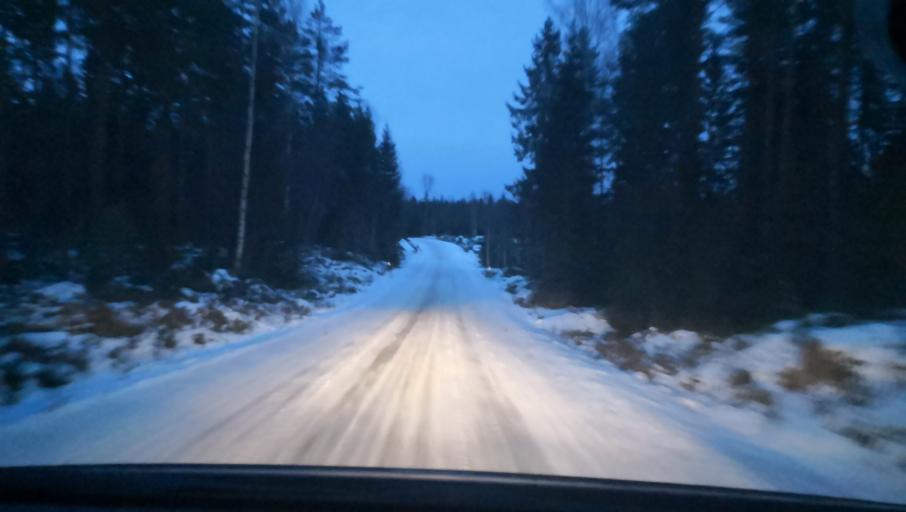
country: SE
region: Dalarna
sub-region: Avesta Kommun
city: Horndal
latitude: 60.2362
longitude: 16.6605
